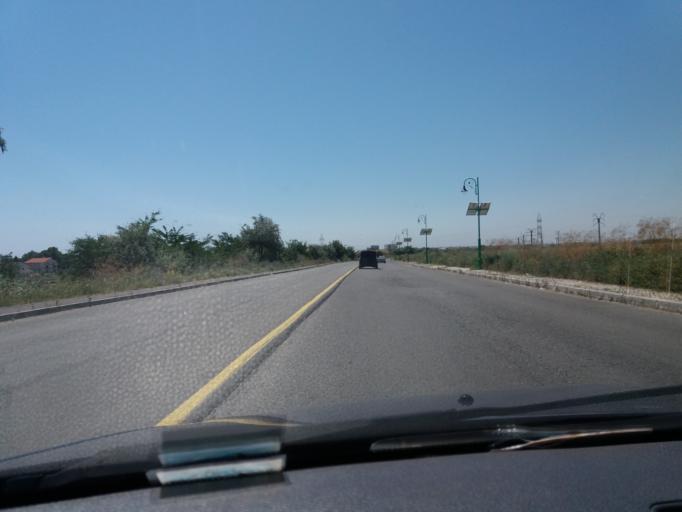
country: RO
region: Constanta
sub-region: Comuna Navodari
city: Navodari
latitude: 44.2968
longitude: 28.6134
